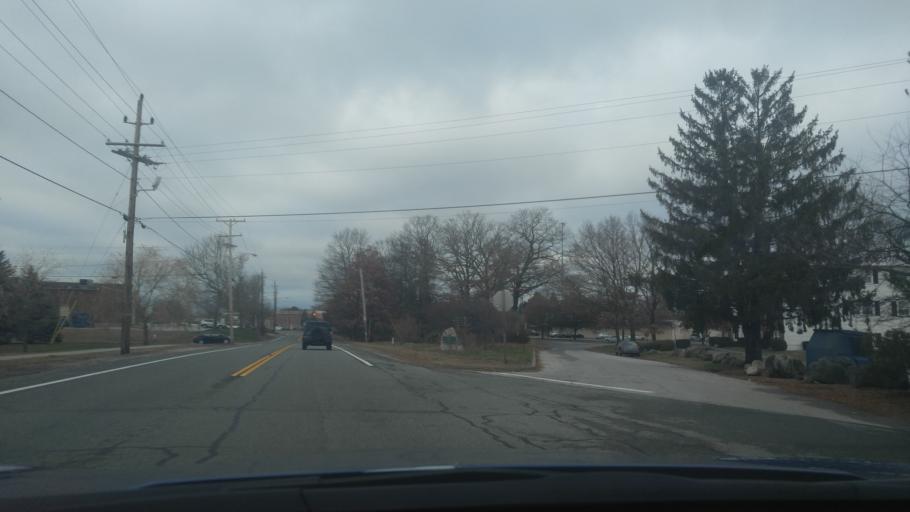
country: US
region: Rhode Island
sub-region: Kent County
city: Warwick
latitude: 41.7069
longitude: -71.3981
